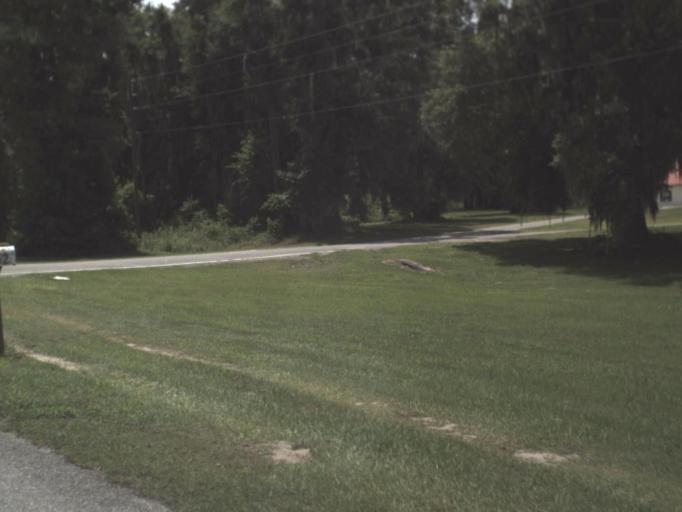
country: US
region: Florida
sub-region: Madison County
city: Madison
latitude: 30.4689
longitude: -83.3742
